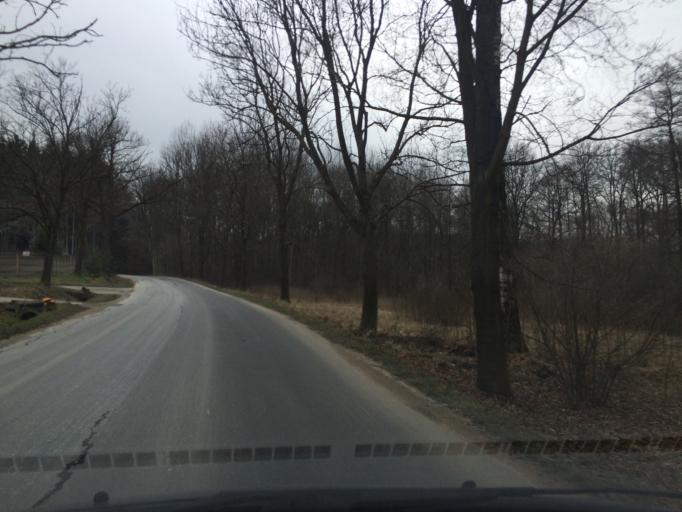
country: PL
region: Lower Silesian Voivodeship
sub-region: Powiat lwowecki
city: Lwowek Slaski
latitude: 51.1204
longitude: 15.5230
